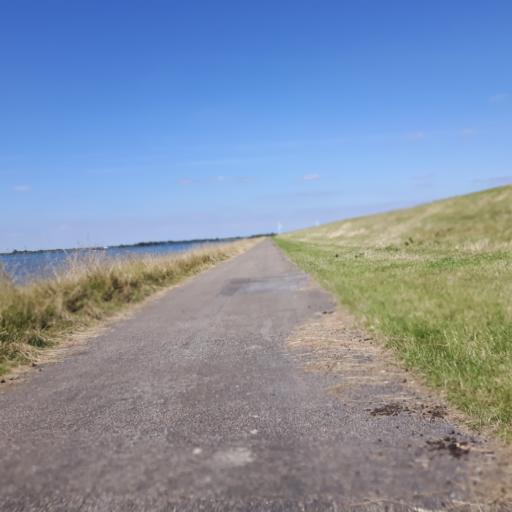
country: NL
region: Zeeland
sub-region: Gemeente Tholen
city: Tholen
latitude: 51.4890
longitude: 4.2266
